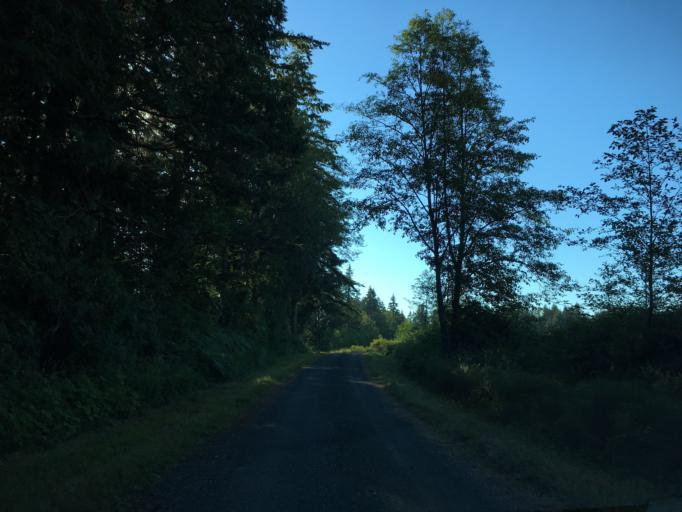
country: US
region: Washington
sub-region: Whatcom County
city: Birch Bay
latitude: 48.9437
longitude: -122.6970
